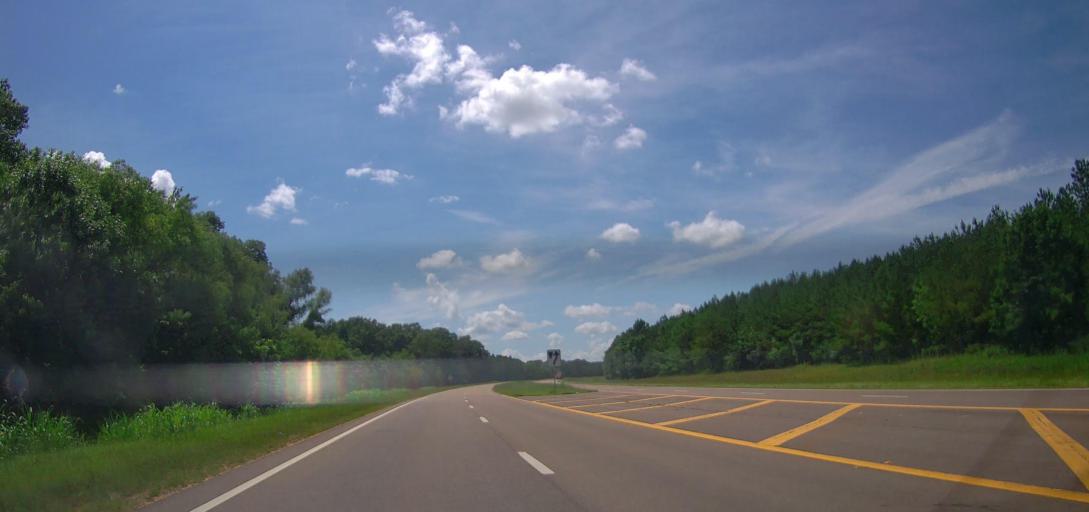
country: US
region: Mississippi
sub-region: Monroe County
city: Aberdeen
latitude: 33.8149
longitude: -88.5720
